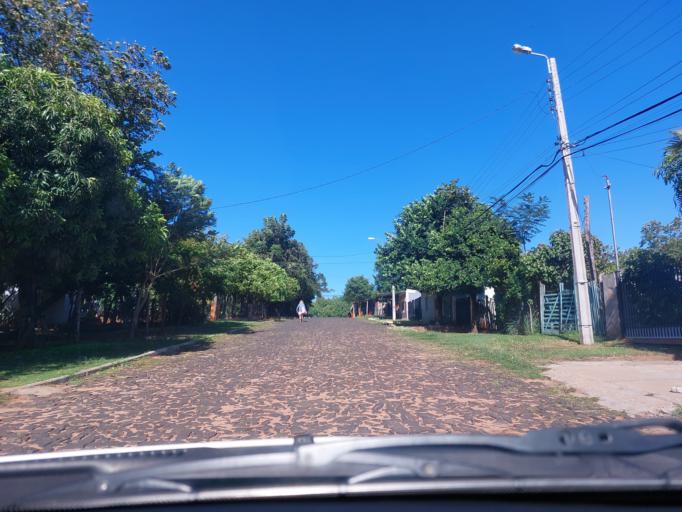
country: PY
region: San Pedro
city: Guayaybi
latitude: -24.6565
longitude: -56.4490
